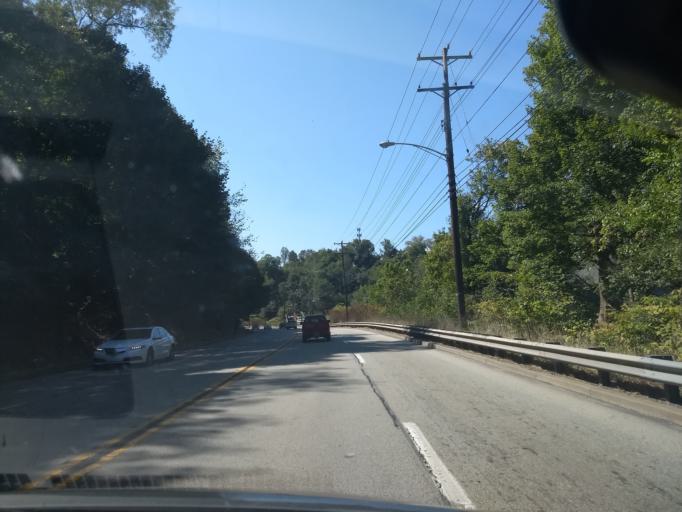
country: US
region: Pennsylvania
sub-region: Allegheny County
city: North Versailles
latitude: 40.3607
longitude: -79.8291
